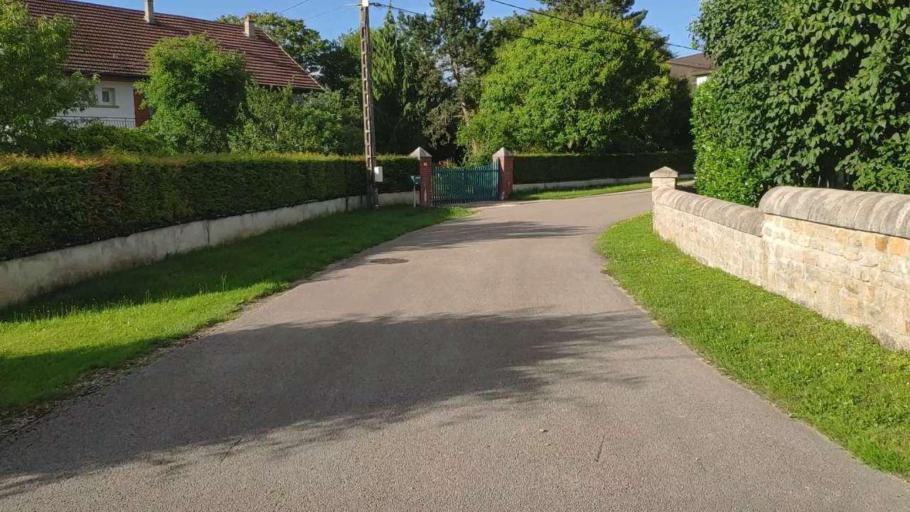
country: FR
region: Franche-Comte
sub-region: Departement du Jura
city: Bletterans
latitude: 46.7693
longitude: 5.5308
